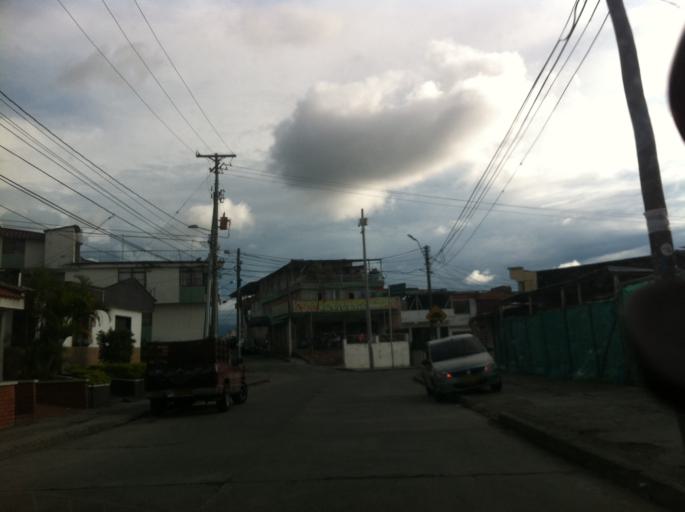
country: CO
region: Quindio
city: Armenia
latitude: 4.5368
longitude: -75.6824
